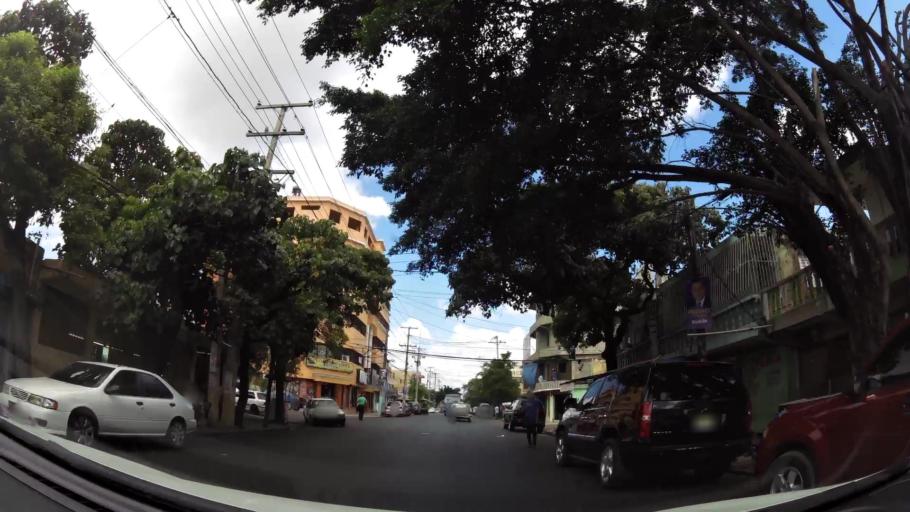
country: DO
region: Nacional
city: Ensanche Luperon
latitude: 18.5040
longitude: -69.8962
